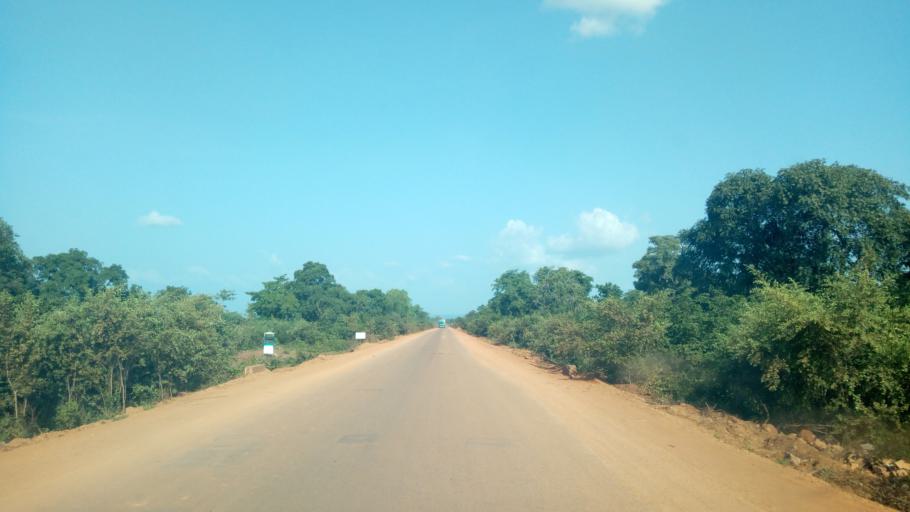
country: ML
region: Sikasso
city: Yorosso
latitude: 12.1850
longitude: -4.8279
